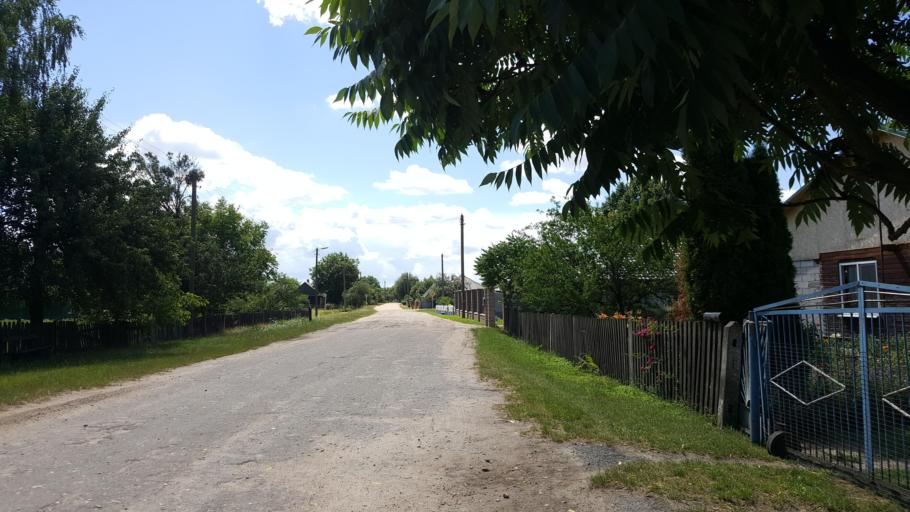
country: BY
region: Brest
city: Kamyanyets
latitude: 52.3339
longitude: 23.9105
